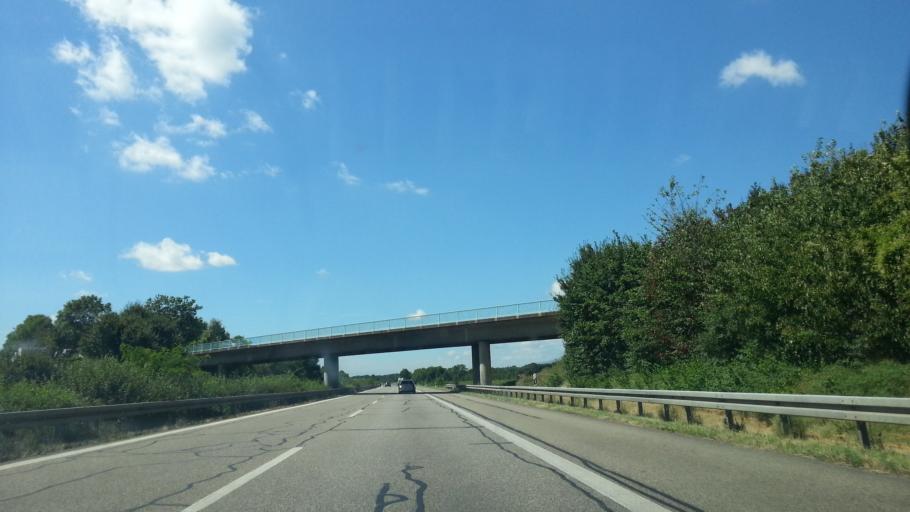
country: DE
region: Baden-Wuerttemberg
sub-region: Freiburg Region
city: Hartheim
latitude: 47.9428
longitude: 7.6305
